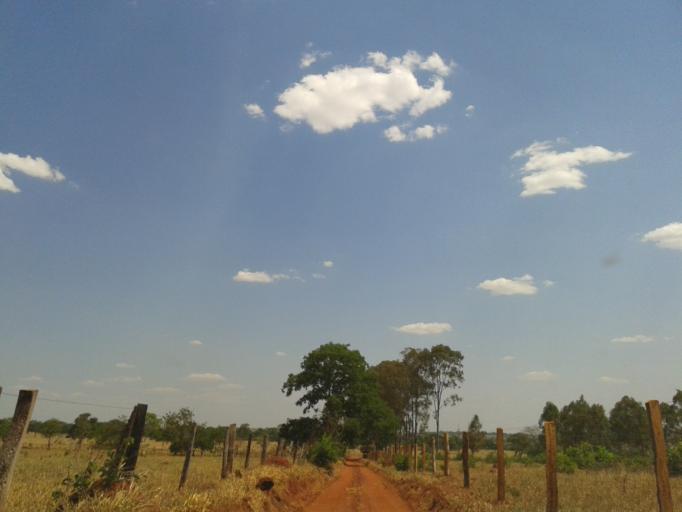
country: BR
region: Minas Gerais
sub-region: Santa Vitoria
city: Santa Vitoria
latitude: -18.8976
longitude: -49.9342
